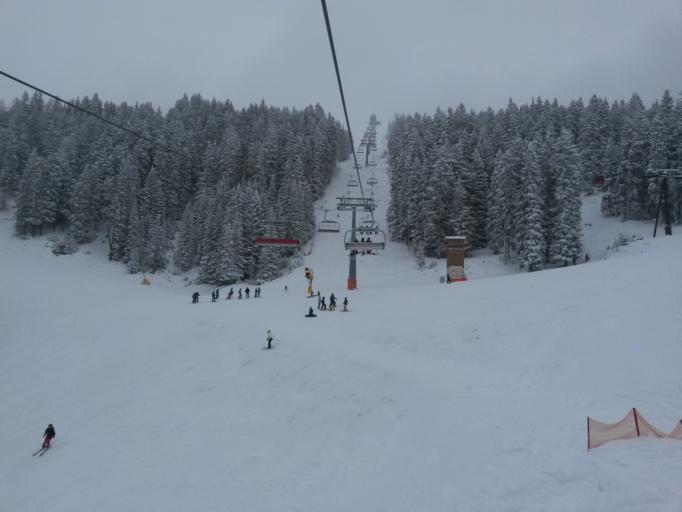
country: AT
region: Salzburg
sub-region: Politischer Bezirk Sankt Johann im Pongau
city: Dorfgastein
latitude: 47.2387
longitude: 13.1368
